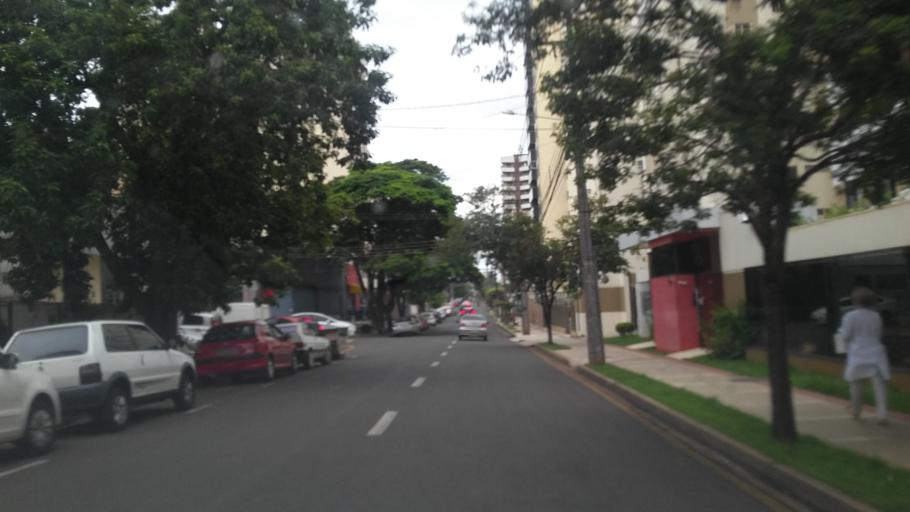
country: BR
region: Parana
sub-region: Londrina
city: Londrina
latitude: -23.3072
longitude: -51.1795
